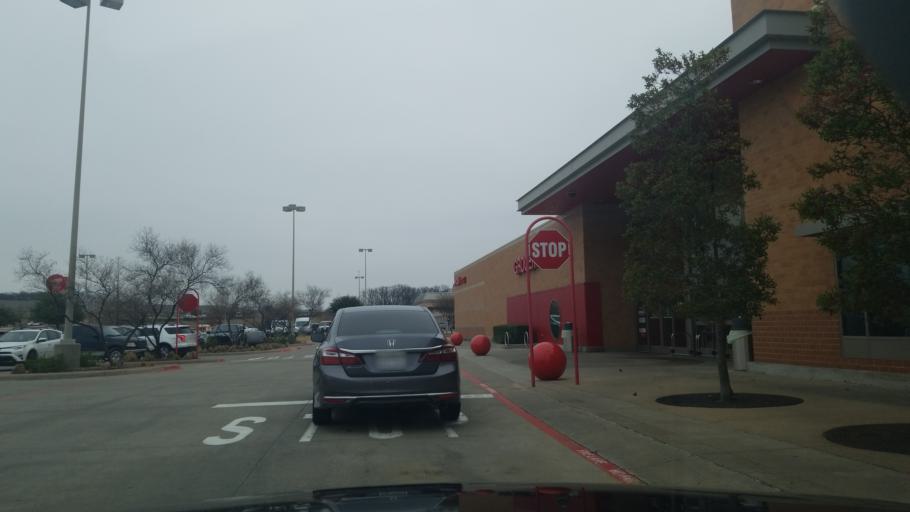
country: US
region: Texas
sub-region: Denton County
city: Denton
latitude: 33.1896
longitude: -97.0984
